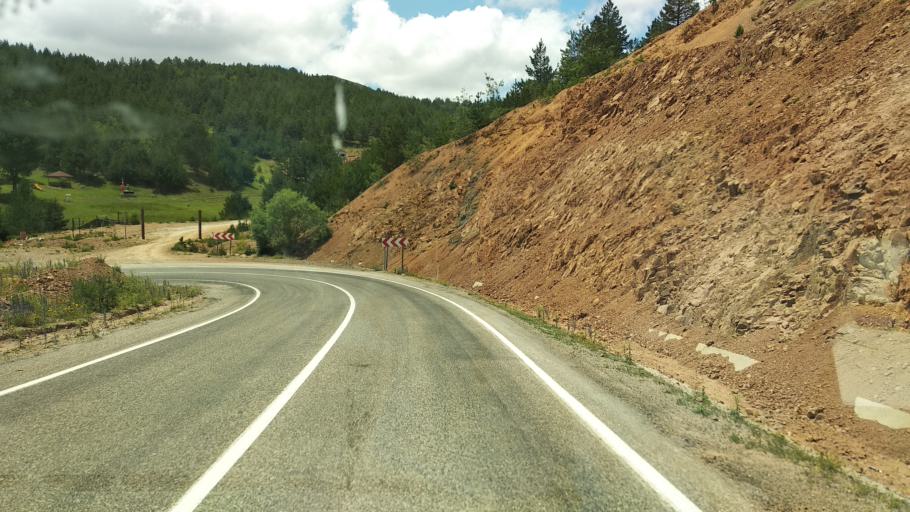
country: TR
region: Gumushane
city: Kose
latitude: 40.2946
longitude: 39.5700
